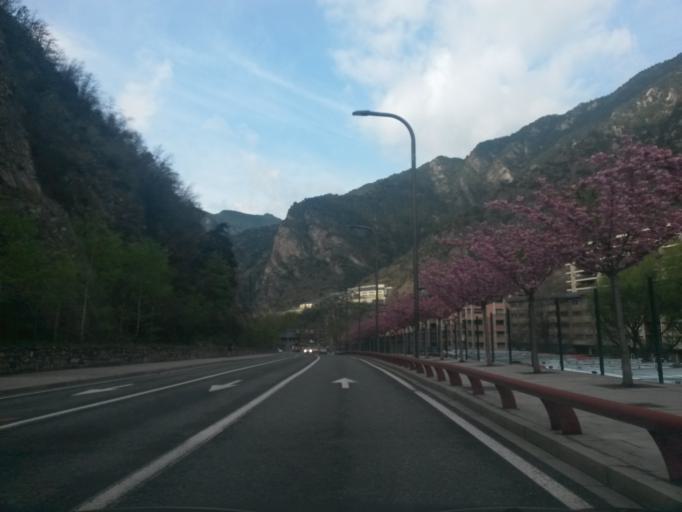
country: AD
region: Andorra la Vella
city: Andorra la Vella
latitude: 42.4923
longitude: 1.4983
